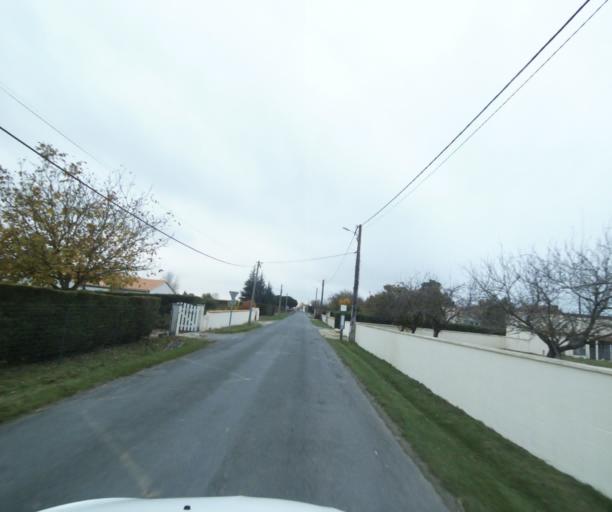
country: FR
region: Poitou-Charentes
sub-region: Departement de la Charente-Maritime
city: Les Gonds
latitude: 45.7373
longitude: -0.6010
